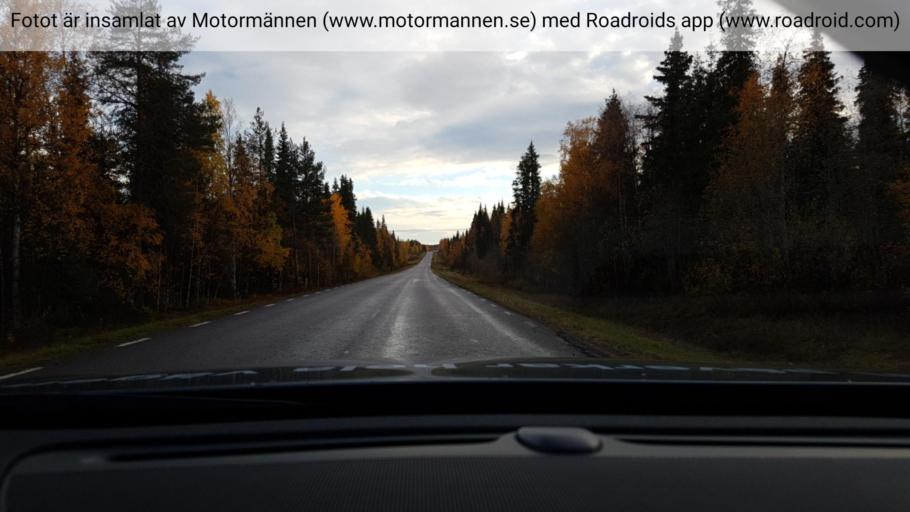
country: SE
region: Norrbotten
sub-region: Overkalix Kommun
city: OEverkalix
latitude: 66.8975
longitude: 22.7731
